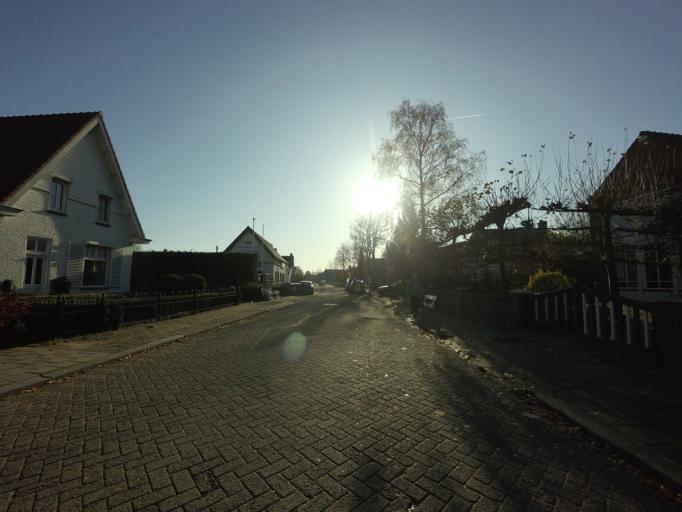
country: NL
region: Gelderland
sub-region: Gemeente Maasdriel
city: Heerewaarden
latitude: 51.7698
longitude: 5.3413
